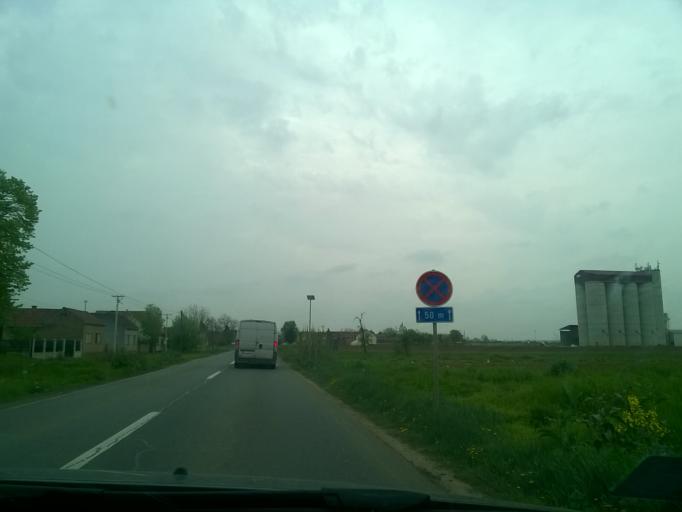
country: RS
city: Platicevo
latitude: 44.8341
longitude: 19.7739
